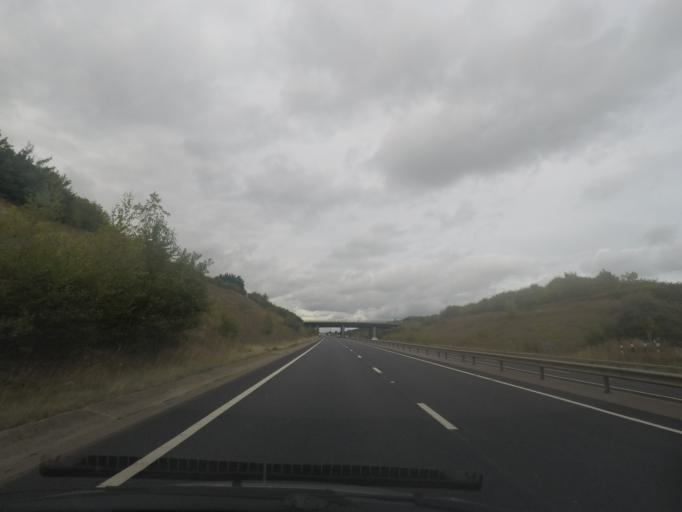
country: GB
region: England
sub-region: West Berkshire
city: Winterbourne
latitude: 51.4539
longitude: -1.3119
